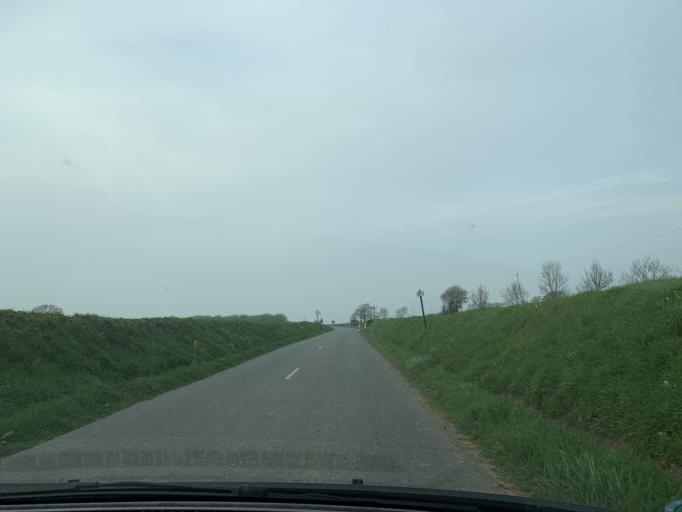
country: FR
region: Nord-Pas-de-Calais
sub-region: Departement du Pas-de-Calais
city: Longfosse
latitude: 50.7050
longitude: 1.7829
